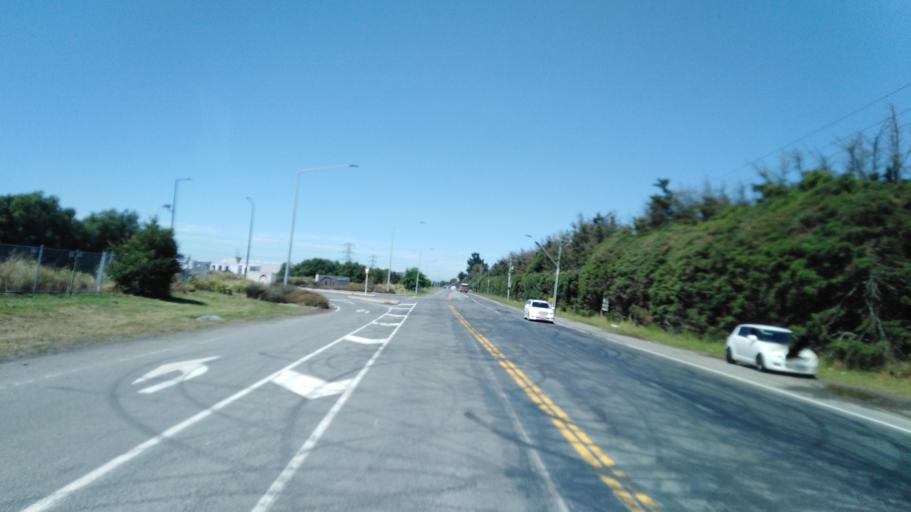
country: NZ
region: Canterbury
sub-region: Selwyn District
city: Prebbleton
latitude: -43.5336
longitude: 172.4967
